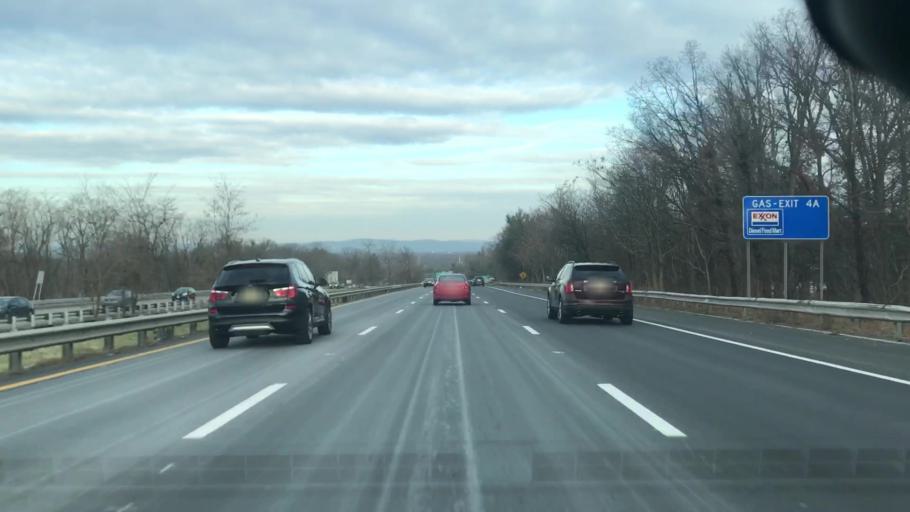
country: US
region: New Jersey
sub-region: Essex County
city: Roseland
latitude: 40.8192
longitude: -74.3155
